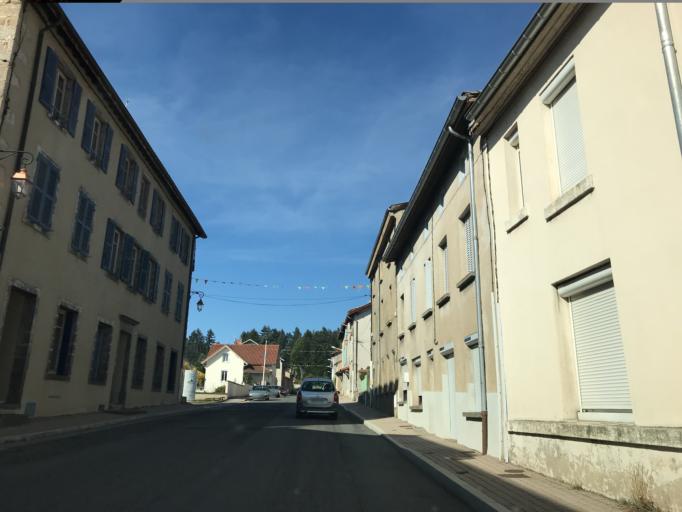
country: FR
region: Rhone-Alpes
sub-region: Departement de la Loire
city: Noiretable
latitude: 45.8182
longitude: 3.7657
